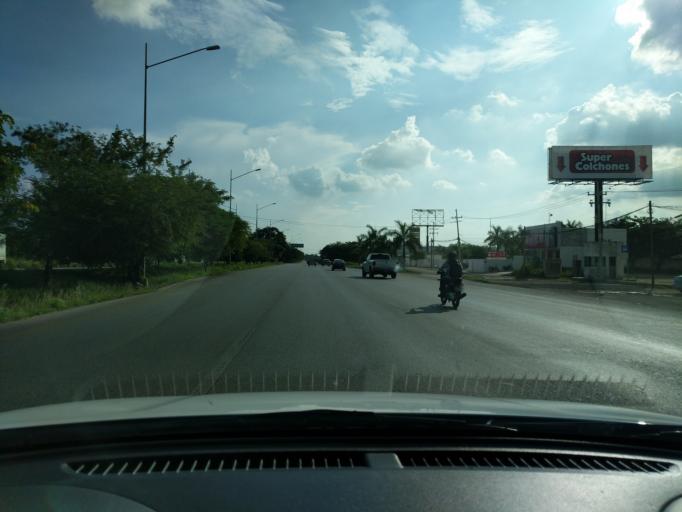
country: MX
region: Yucatan
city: Itzincab Palomeque
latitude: 20.9556
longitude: -89.6992
